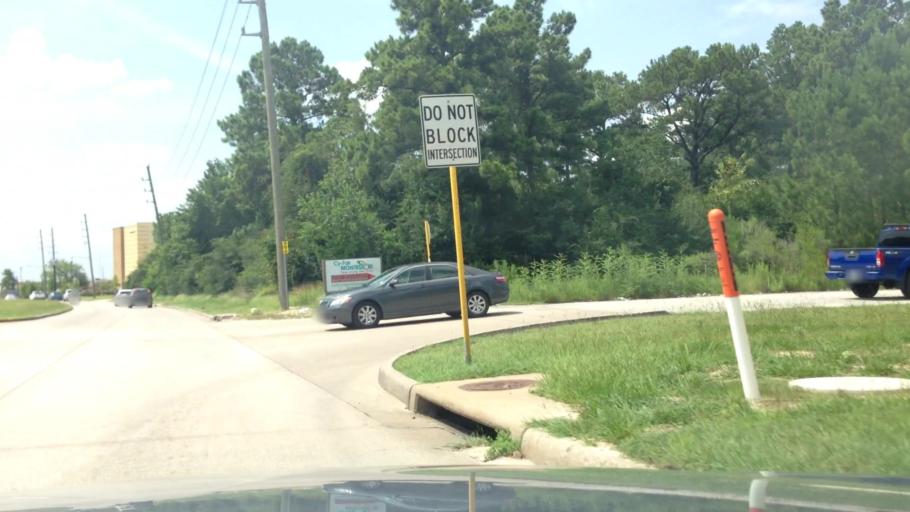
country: US
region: Texas
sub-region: Harris County
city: Jersey Village
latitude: 29.9339
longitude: -95.5460
